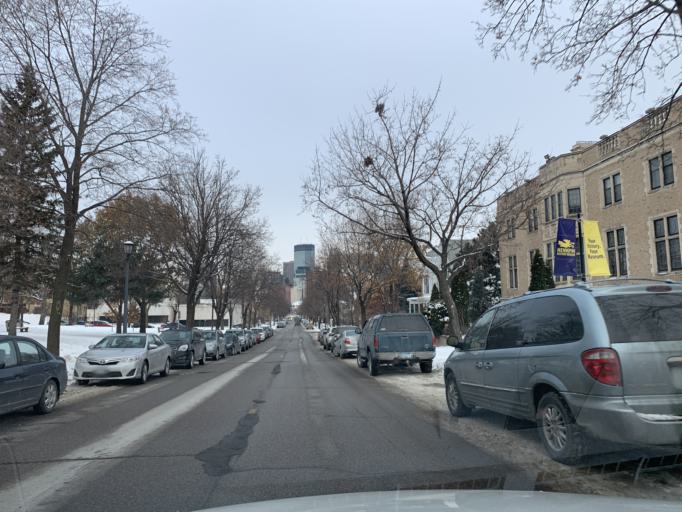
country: US
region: Minnesota
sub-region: Hennepin County
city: Minneapolis
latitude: 44.9598
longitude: -93.2727
